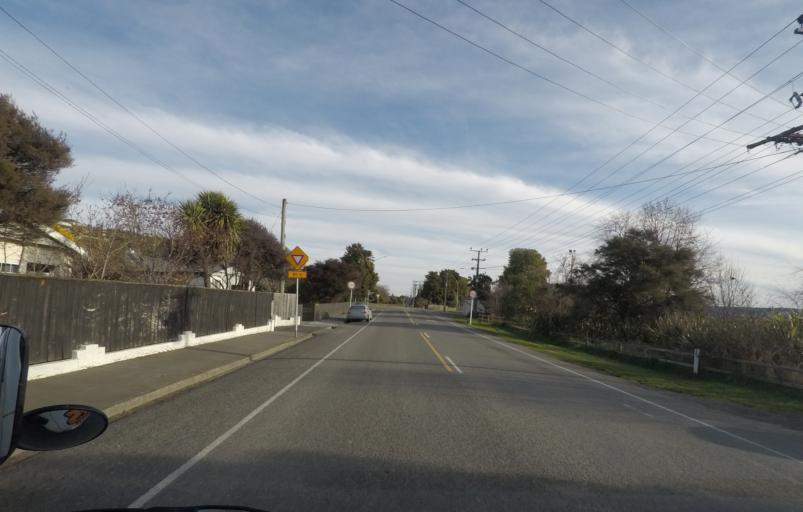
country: NZ
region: Tasman
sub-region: Tasman District
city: Brightwater
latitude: -41.3770
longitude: 173.1027
